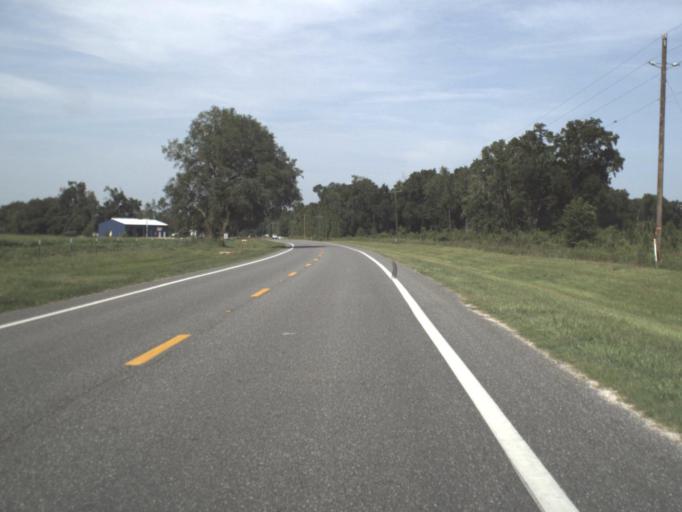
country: US
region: Florida
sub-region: Lafayette County
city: Mayo
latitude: 30.1793
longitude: -83.1402
